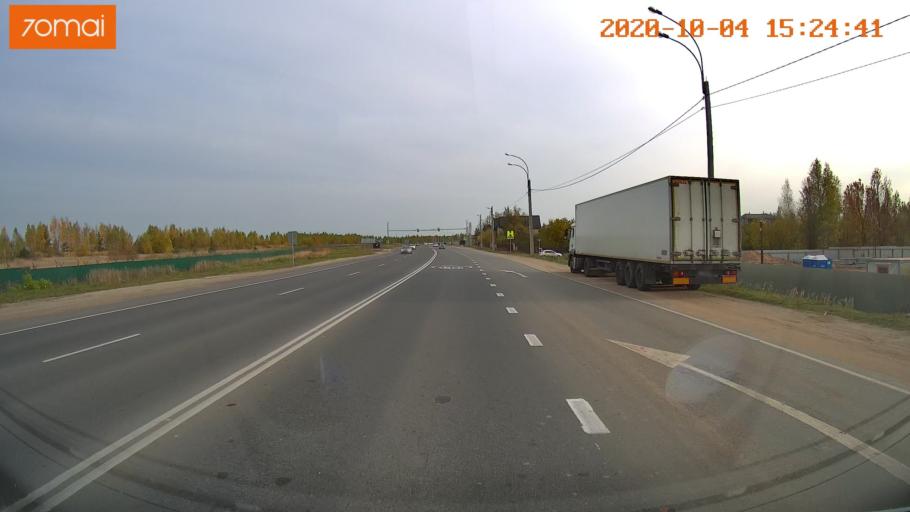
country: RU
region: Ivanovo
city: Bogorodskoye
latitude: 57.0618
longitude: 40.9569
